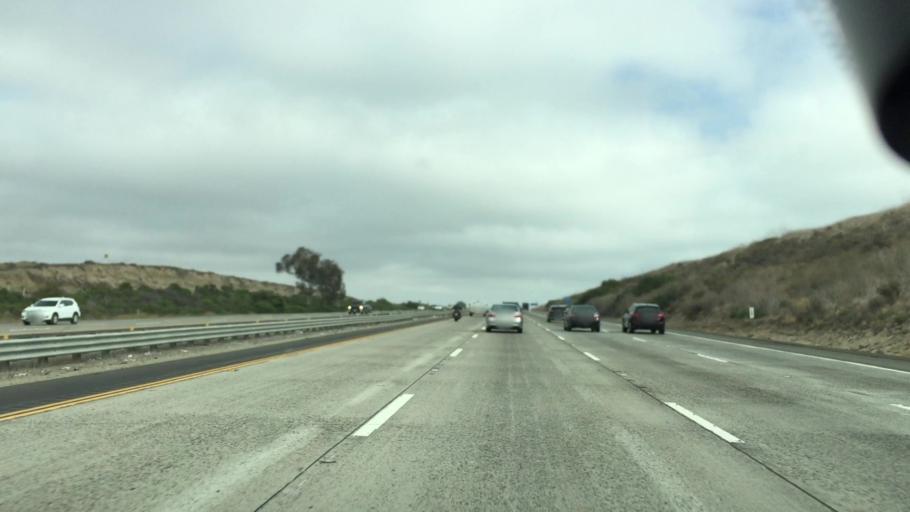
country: US
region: California
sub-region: San Diego County
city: Camp Pendleton South
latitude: 33.2899
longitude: -117.4558
